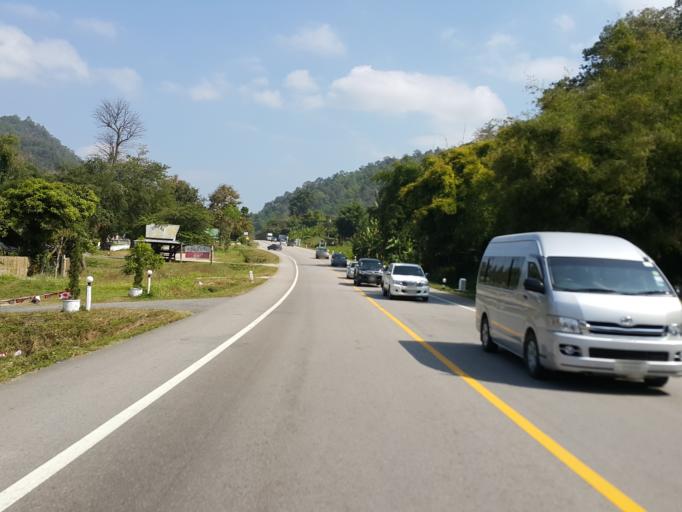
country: TH
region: Chiang Mai
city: Mae On
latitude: 19.0397
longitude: 99.3344
